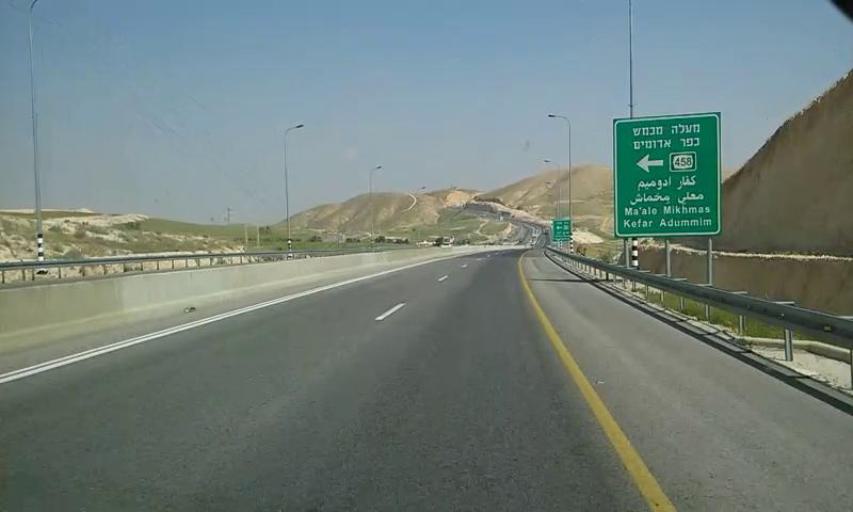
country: PS
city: Az Za`ayyim
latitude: 31.8139
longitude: 35.3463
